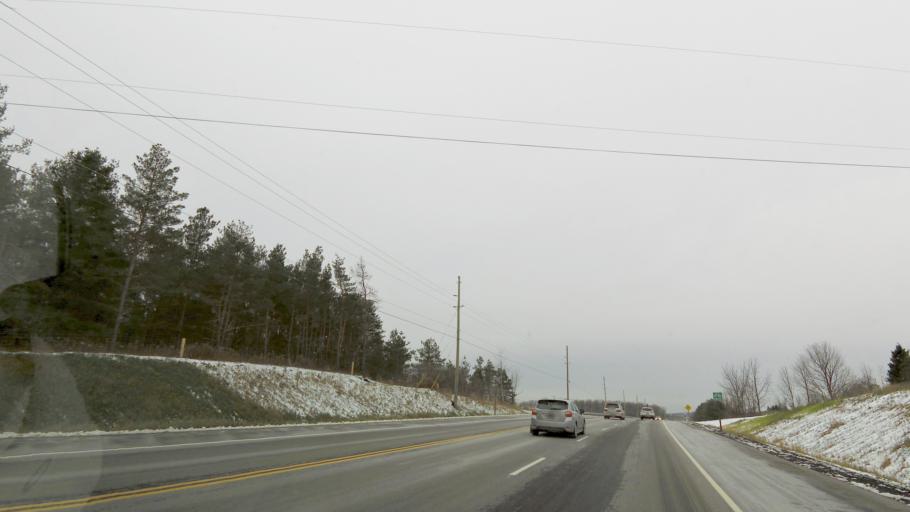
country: CA
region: Ontario
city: Newmarket
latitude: 44.0828
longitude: -79.5147
